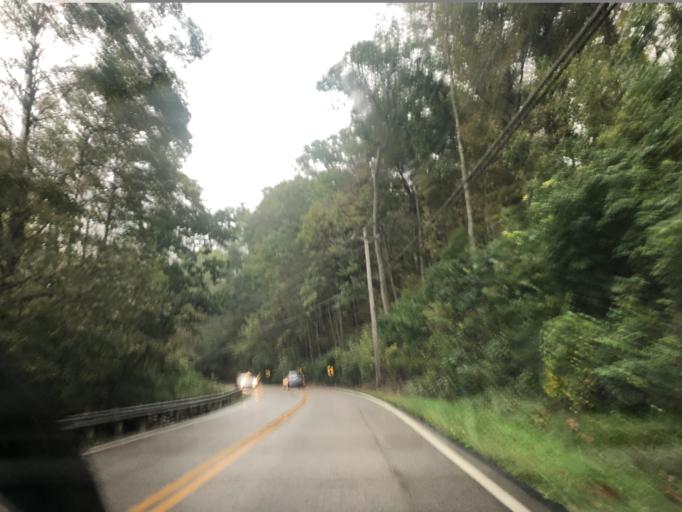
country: US
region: Ohio
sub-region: Clermont County
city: Mulberry
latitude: 39.2058
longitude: -84.2473
